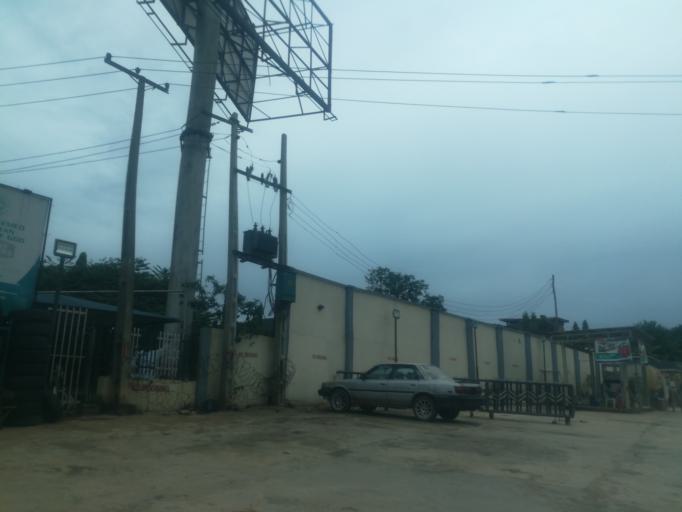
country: NG
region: Oyo
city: Ibadan
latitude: 7.3373
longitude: 3.8948
